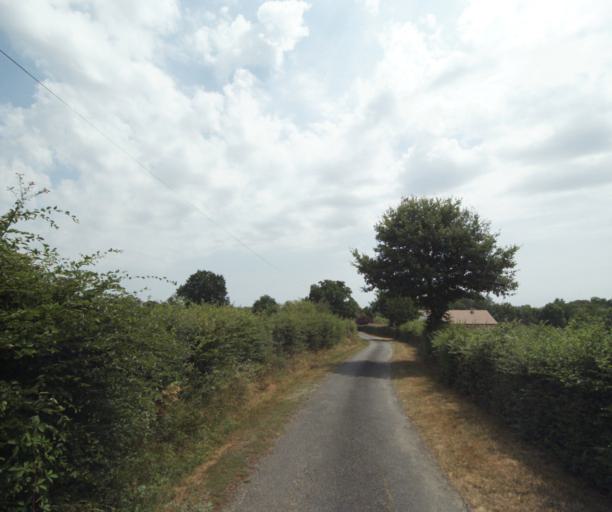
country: FR
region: Bourgogne
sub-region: Departement de Saone-et-Loire
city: Gueugnon
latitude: 46.5829
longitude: 4.0282
